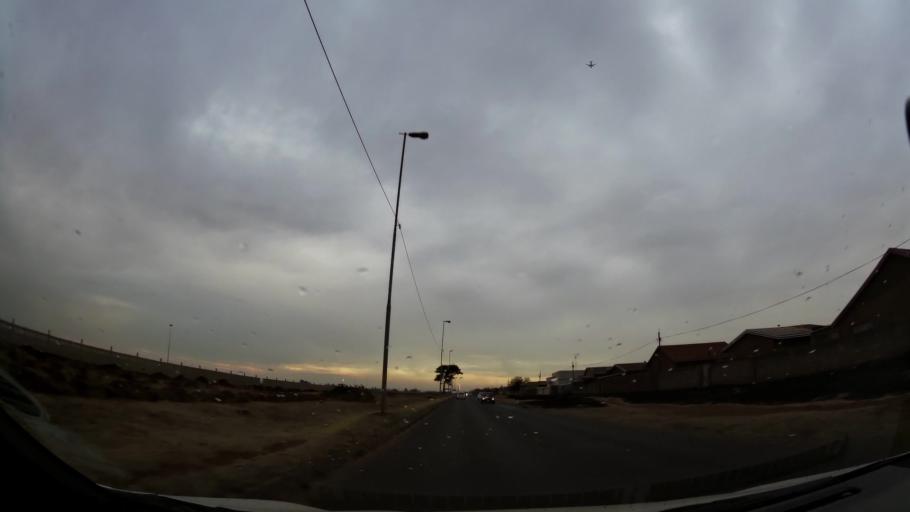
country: ZA
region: Gauteng
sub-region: Ekurhuleni Metropolitan Municipality
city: Germiston
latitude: -26.3690
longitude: 28.1842
